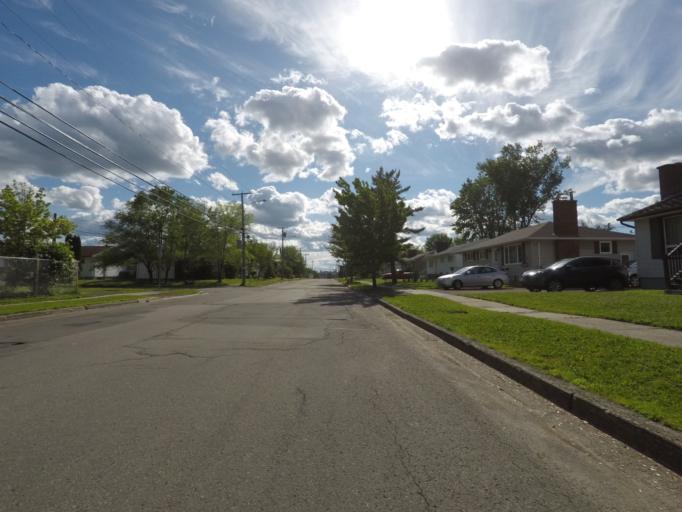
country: CA
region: New Brunswick
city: Moncton
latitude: 46.1034
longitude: -64.8274
